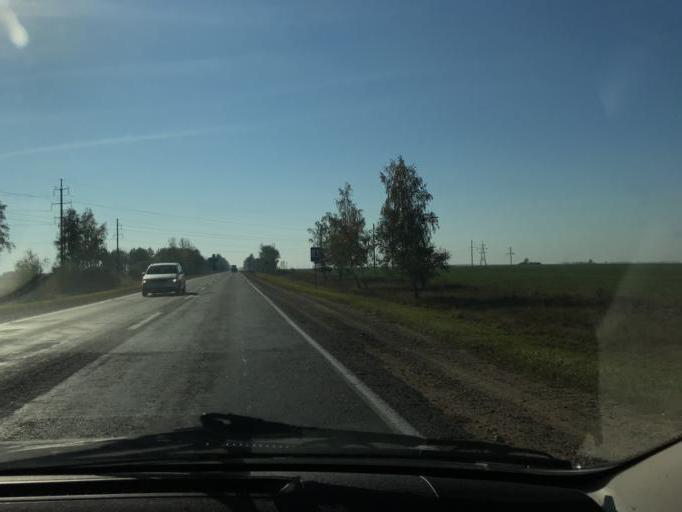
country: BY
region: Minsk
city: Salihorsk
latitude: 52.9070
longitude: 27.4781
